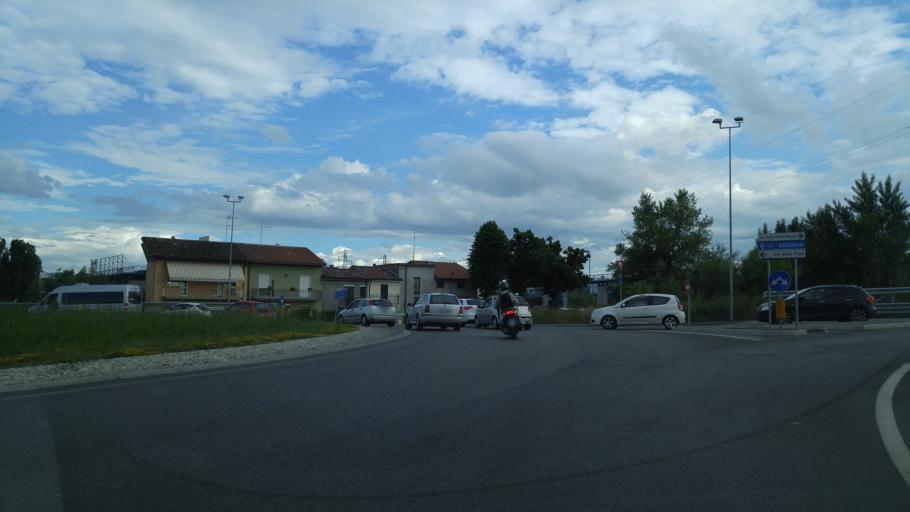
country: IT
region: Emilia-Romagna
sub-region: Provincia di Rimini
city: Rimini
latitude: 44.0441
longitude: 12.5593
